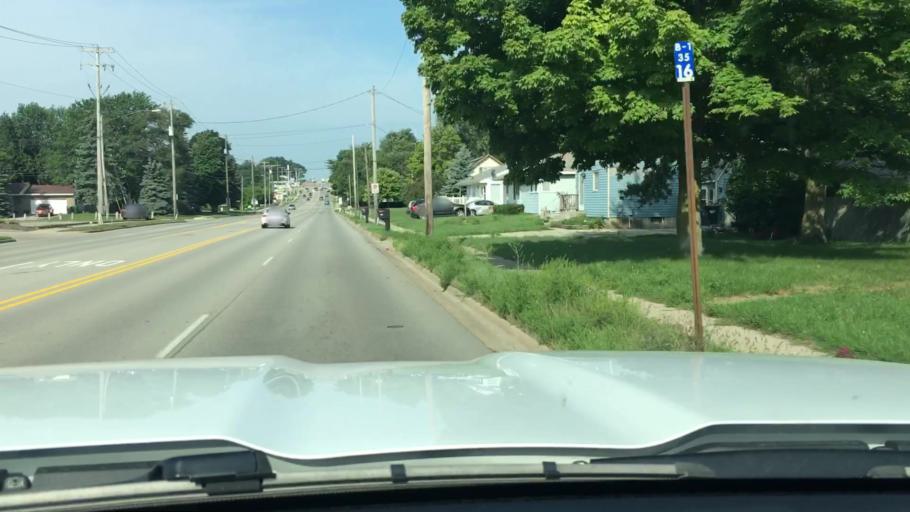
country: US
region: Michigan
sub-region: Kent County
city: Cutlerville
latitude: 42.8409
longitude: -85.6689
